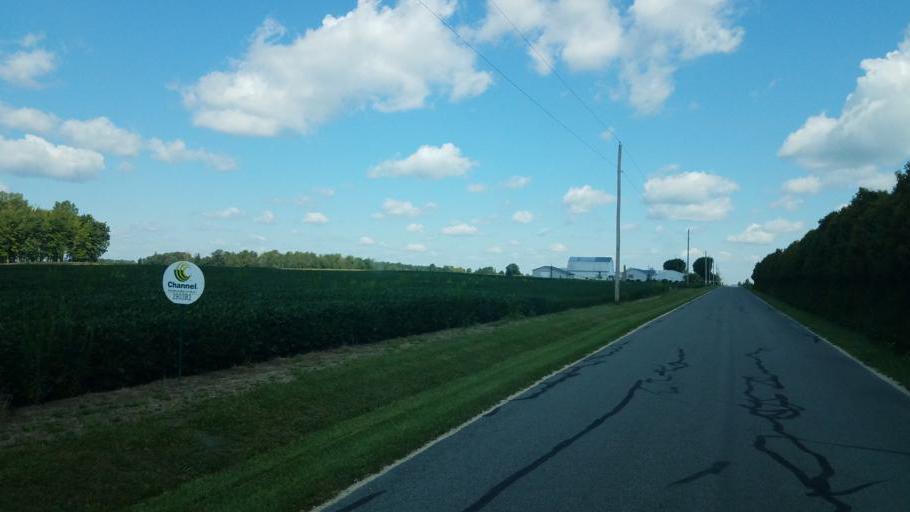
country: US
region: Ohio
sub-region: Wyandot County
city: Carey
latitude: 41.0196
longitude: -83.3244
